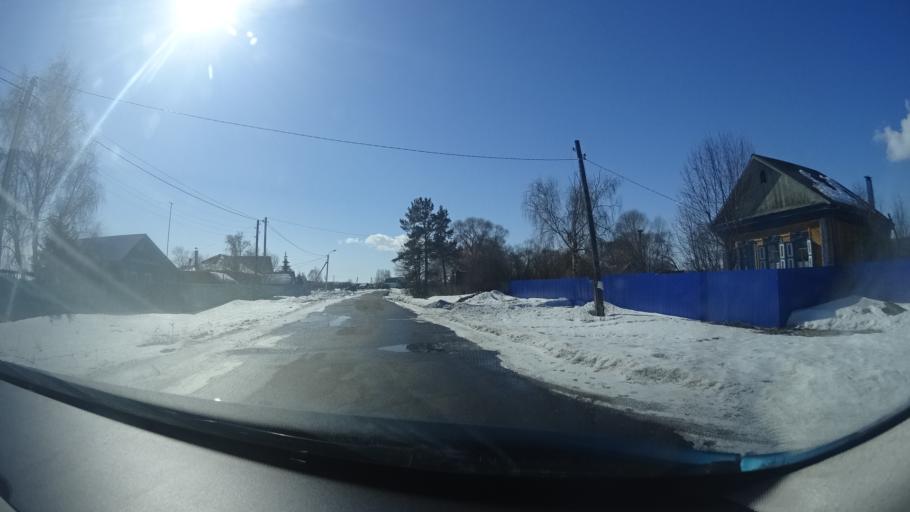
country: RU
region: Bashkortostan
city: Avdon
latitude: 54.5825
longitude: 55.8575
